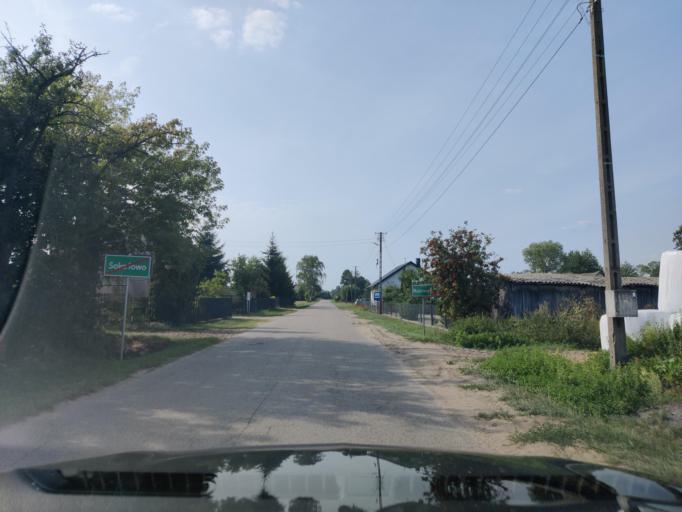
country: PL
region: Masovian Voivodeship
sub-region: Powiat pultuski
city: Obryte
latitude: 52.7648
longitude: 21.2889
